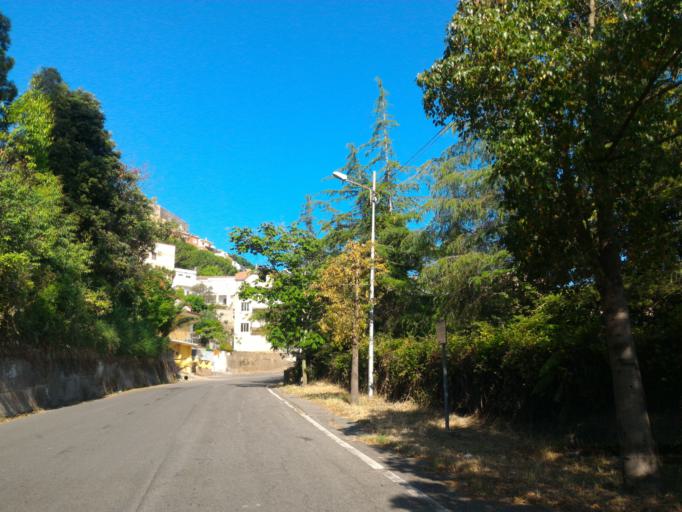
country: IT
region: Calabria
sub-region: Provincia di Crotone
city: Ciro
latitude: 39.3811
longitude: 17.0679
